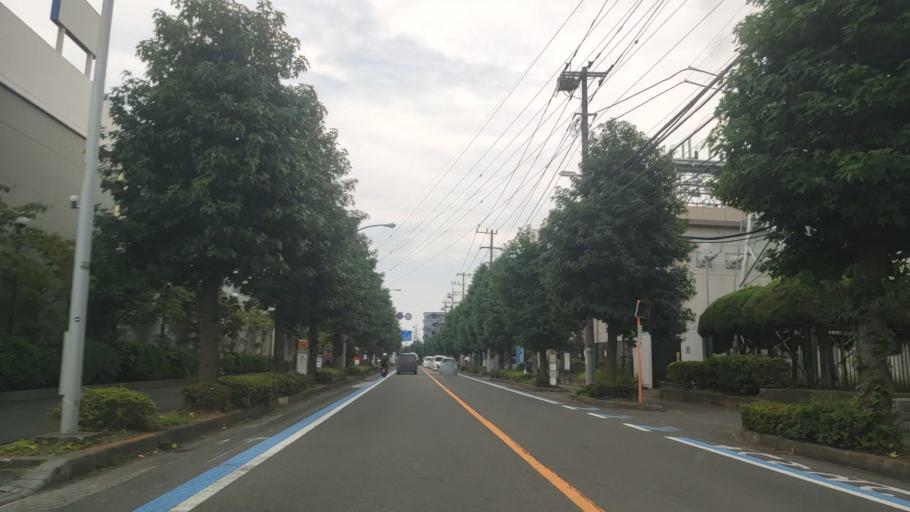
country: JP
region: Kanagawa
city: Minami-rinkan
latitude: 35.5038
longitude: 139.4492
